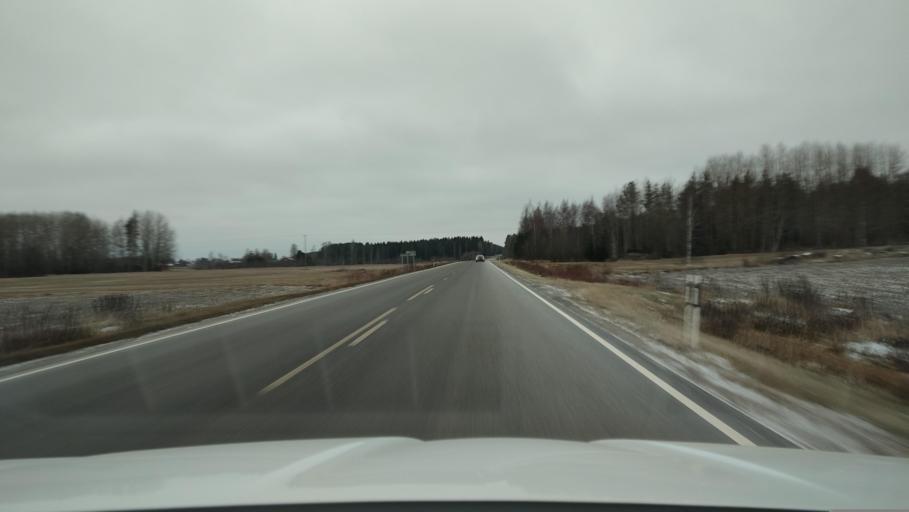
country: FI
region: Ostrobothnia
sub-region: Sydosterbotten
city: Naerpes
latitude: 62.5444
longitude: 21.4689
